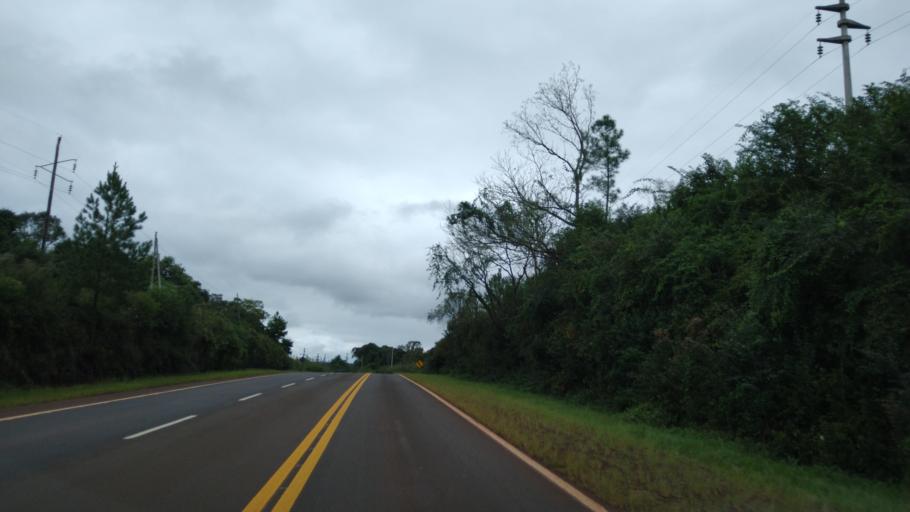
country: AR
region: Misiones
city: Capiovi
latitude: -26.9578
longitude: -55.1002
